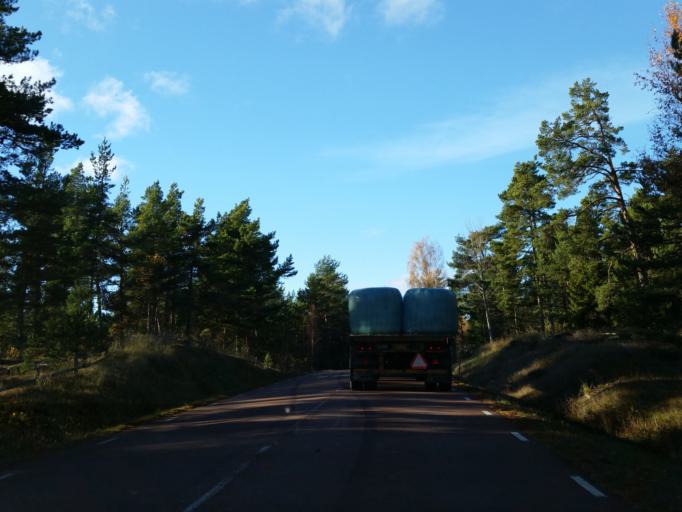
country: AX
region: Alands landsbygd
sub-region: Geta
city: Geta
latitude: 60.3655
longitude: 19.7825
